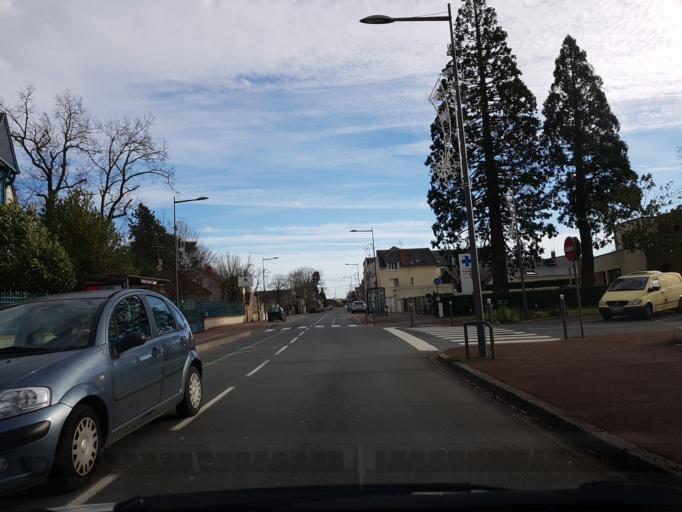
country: FR
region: Centre
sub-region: Departement du Loiret
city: Saint-Jean-le-Blanc
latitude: 47.8920
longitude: 1.9188
